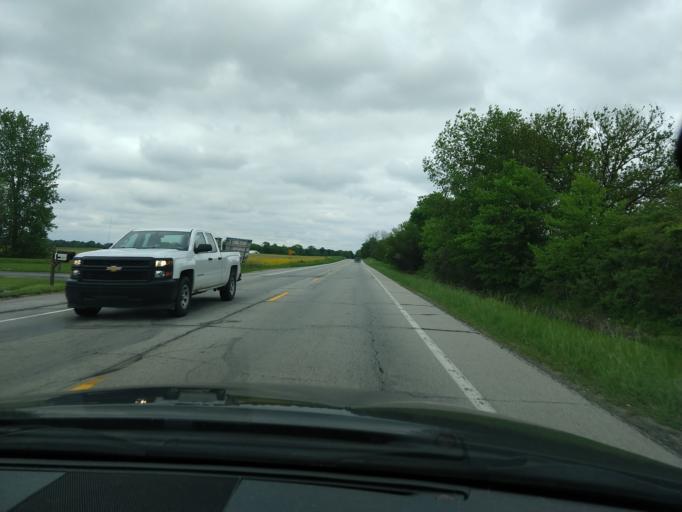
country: US
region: Indiana
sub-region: Hamilton County
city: Noblesville
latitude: 40.0467
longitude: -85.9564
